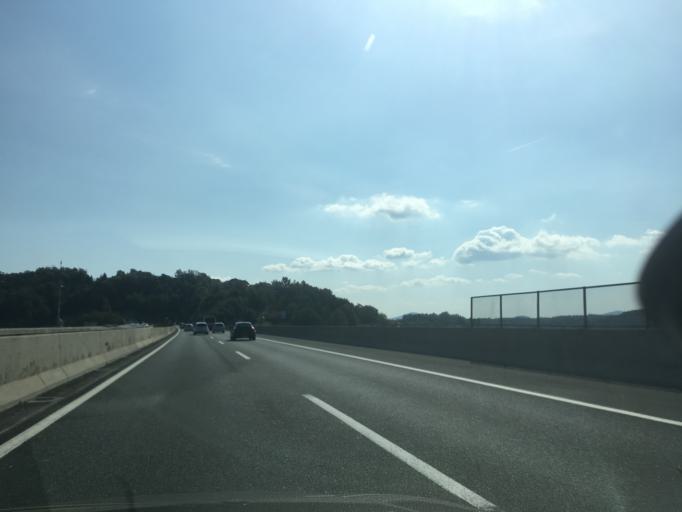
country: SI
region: Skofljica
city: Skofljica
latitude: 45.9890
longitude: 14.5941
